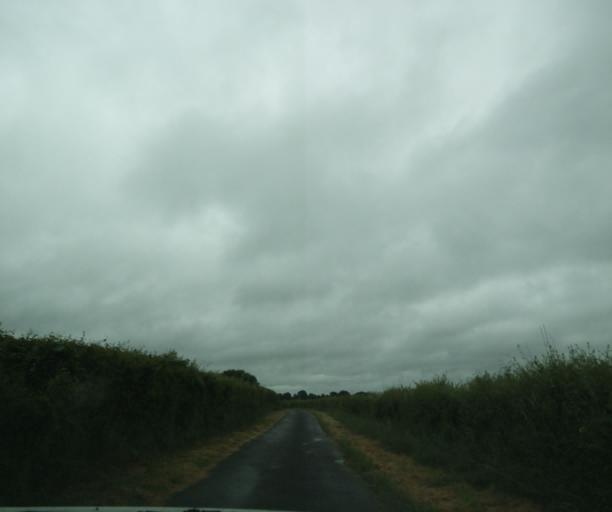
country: FR
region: Bourgogne
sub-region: Departement de Saone-et-Loire
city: Palinges
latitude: 46.5576
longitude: 4.1998
